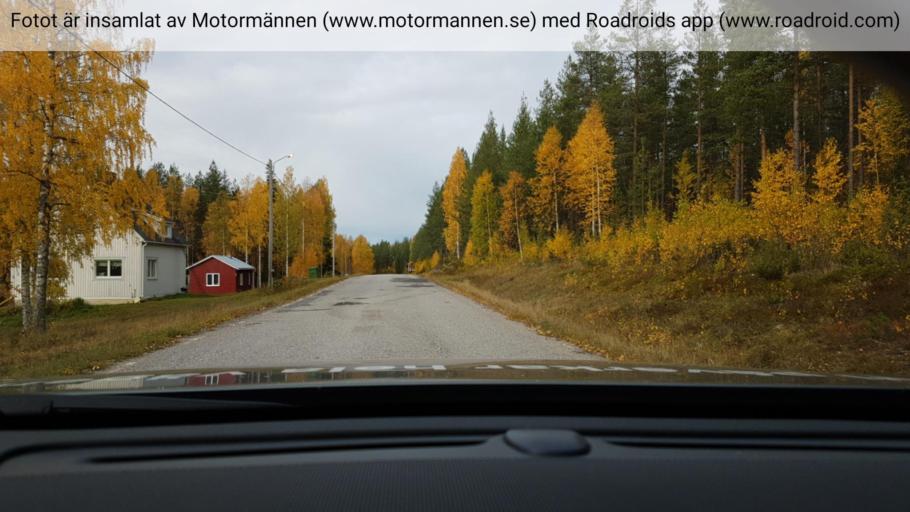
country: SE
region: Norrbotten
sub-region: Overkalix Kommun
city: OEverkalix
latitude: 66.2531
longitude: 23.1249
